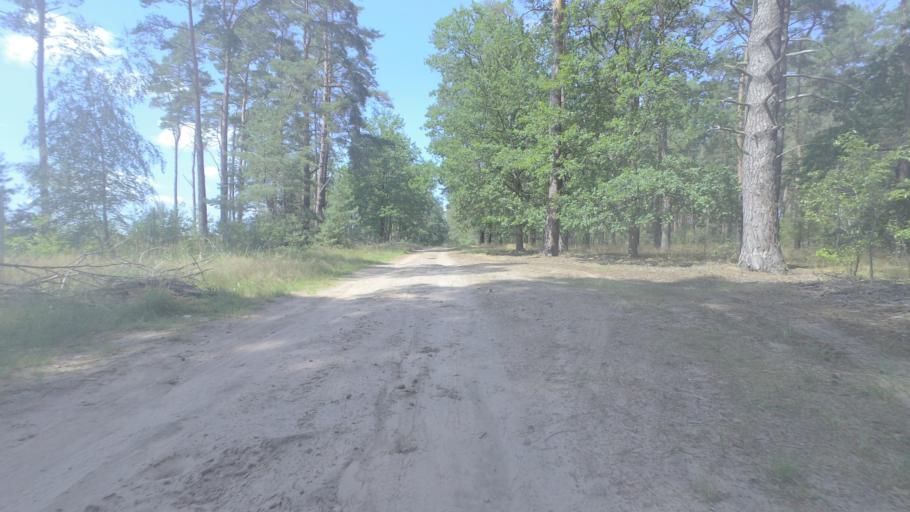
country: DE
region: Brandenburg
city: Am Mellensee
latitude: 52.2315
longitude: 13.3873
